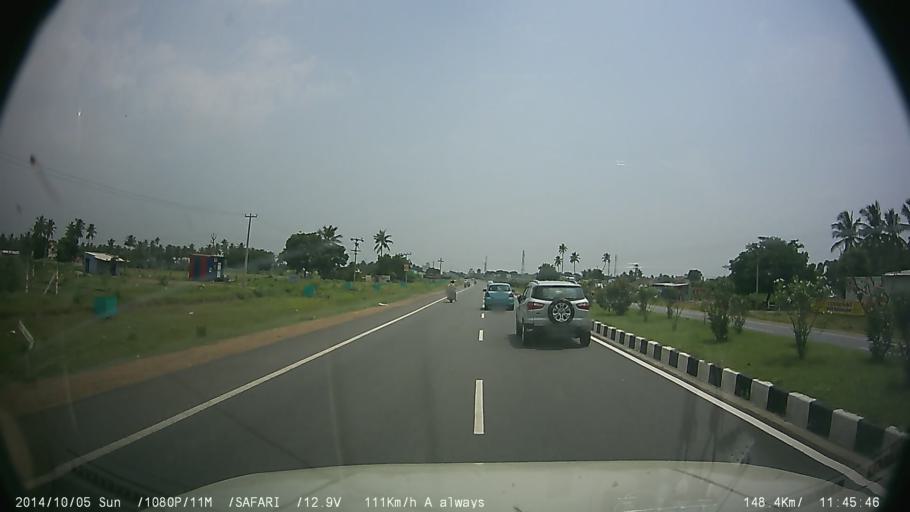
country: IN
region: Tamil Nadu
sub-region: Salem
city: Attur
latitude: 11.5915
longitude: 78.6598
